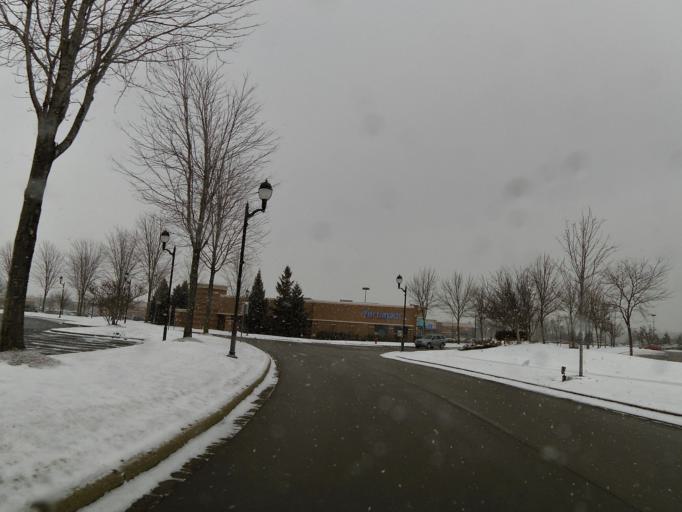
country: US
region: Minnesota
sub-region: Washington County
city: Woodbury
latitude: 44.9412
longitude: -92.9387
